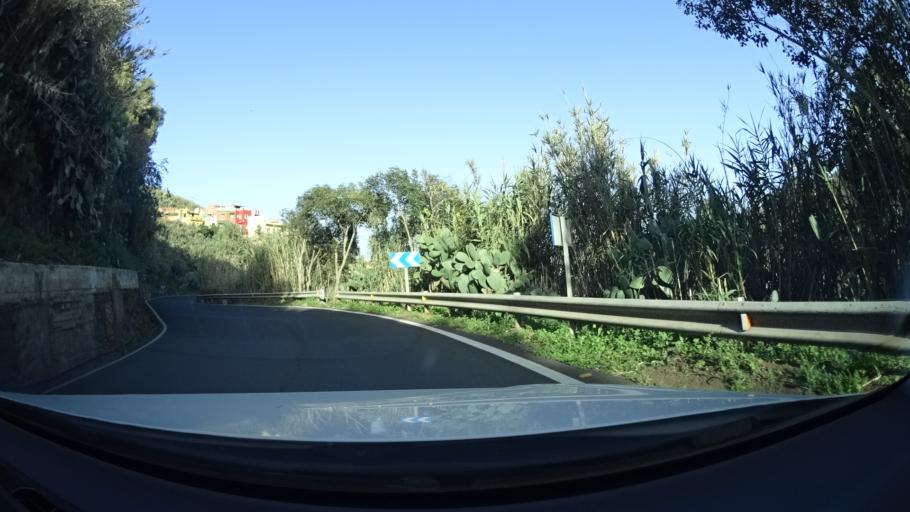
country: ES
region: Canary Islands
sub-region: Provincia de Las Palmas
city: Teror
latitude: 28.0582
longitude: -15.5586
